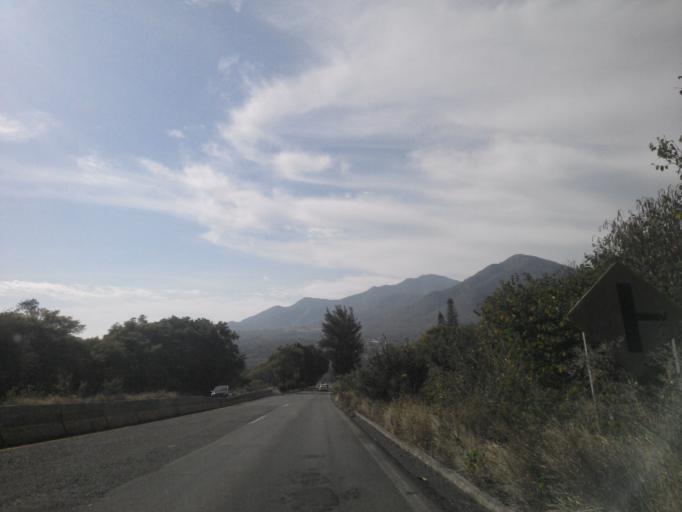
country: MX
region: Jalisco
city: Ixtlahuacan de los Membrillos
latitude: 20.3272
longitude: -103.1876
